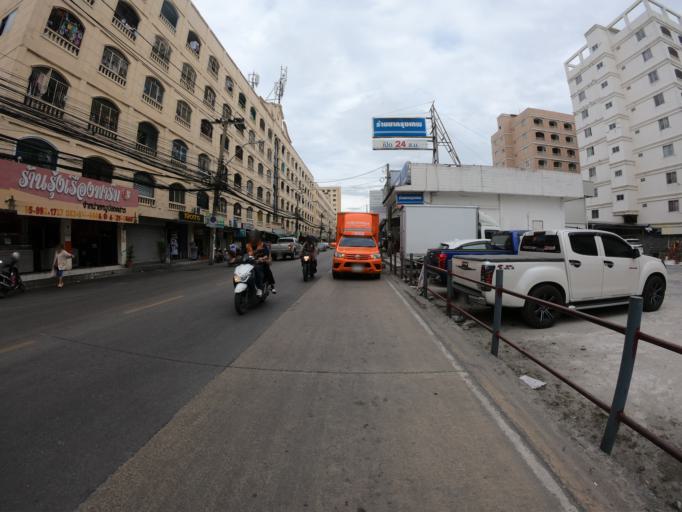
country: TH
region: Bangkok
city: Bang Na
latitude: 13.6727
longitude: 100.6814
